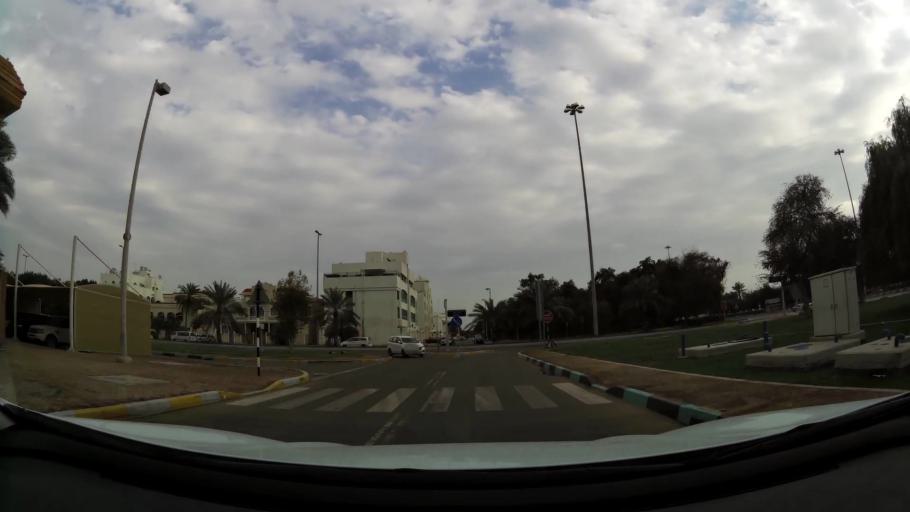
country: AE
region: Abu Dhabi
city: Abu Dhabi
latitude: 24.4428
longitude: 54.3975
